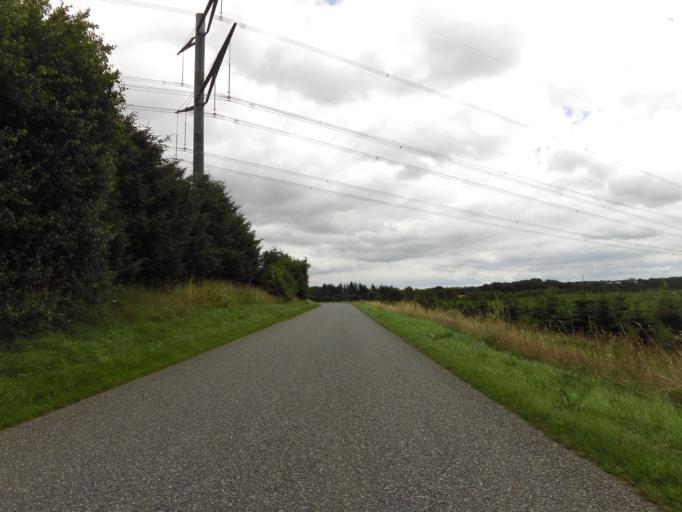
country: DK
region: South Denmark
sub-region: Haderslev Kommune
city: Gram
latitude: 55.2986
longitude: 9.1563
